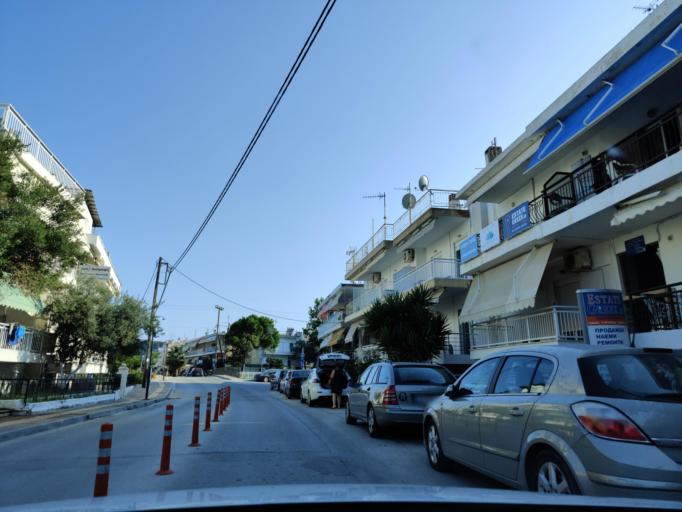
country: GR
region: East Macedonia and Thrace
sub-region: Nomos Kavalas
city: Nea Peramos
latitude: 40.8334
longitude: 24.3045
